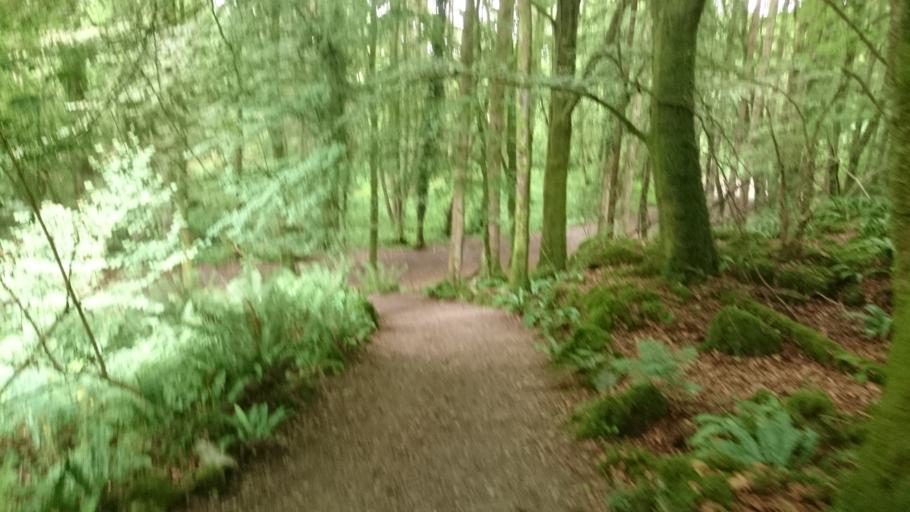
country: IE
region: Munster
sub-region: An Clar
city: Sixmilebridge
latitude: 52.8117
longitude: -8.7958
